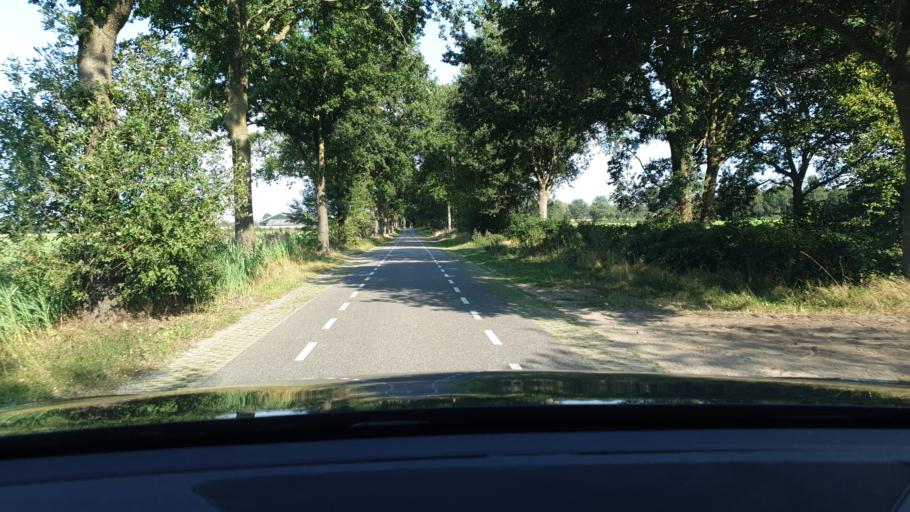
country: NL
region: North Brabant
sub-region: Gemeente Bernheze
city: Heesch
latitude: 51.7134
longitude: 5.5369
